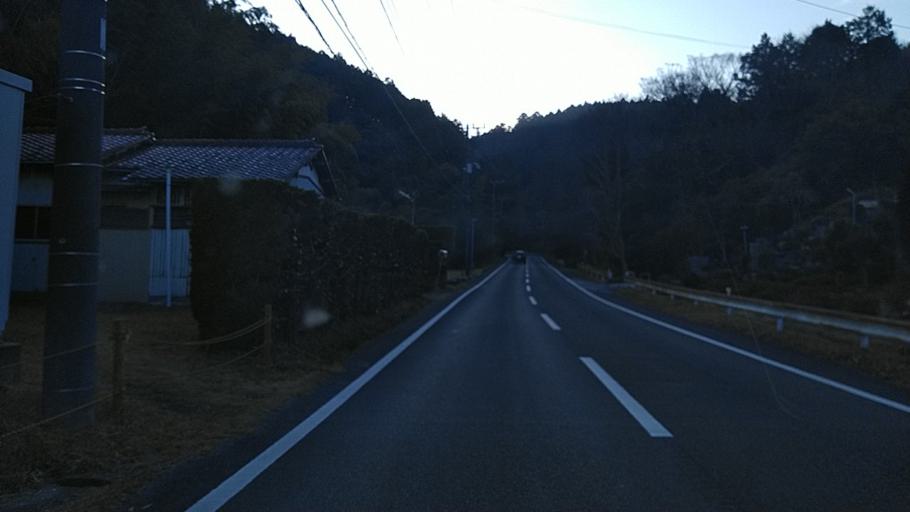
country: JP
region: Chiba
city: Kimitsu
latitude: 35.2687
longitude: 139.9230
